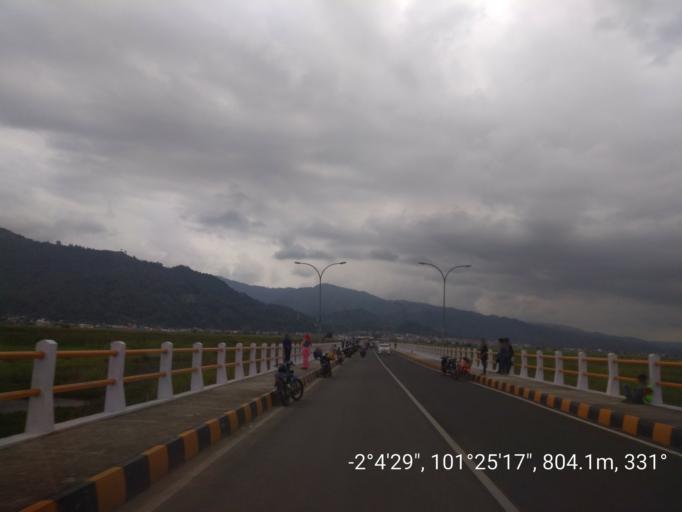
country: ID
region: Jambi
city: Sungai Penuh
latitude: -2.0747
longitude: 101.4212
